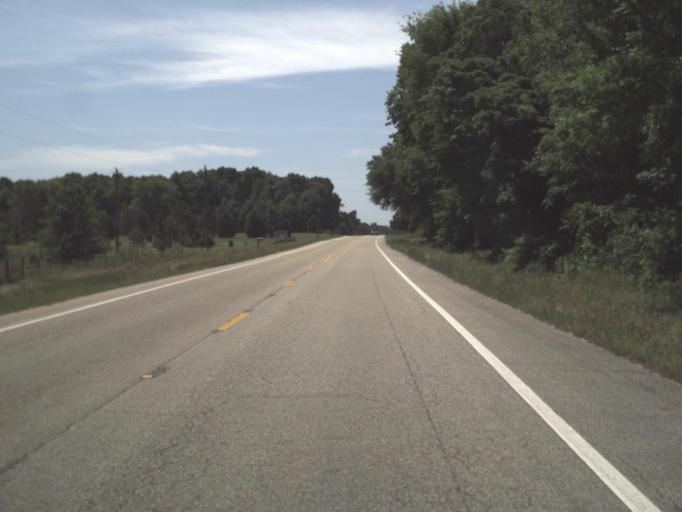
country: US
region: Florida
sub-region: Jackson County
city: Marianna
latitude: 30.5879
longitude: -85.1819
